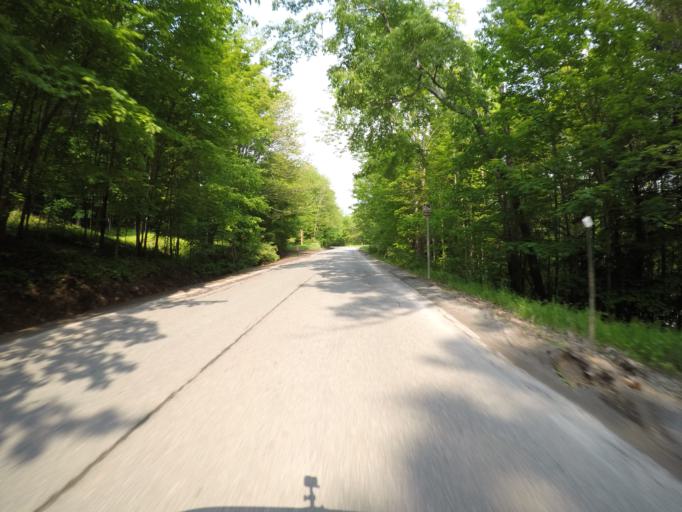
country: US
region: New York
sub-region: Sullivan County
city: Livingston Manor
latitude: 42.1118
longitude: -74.7485
